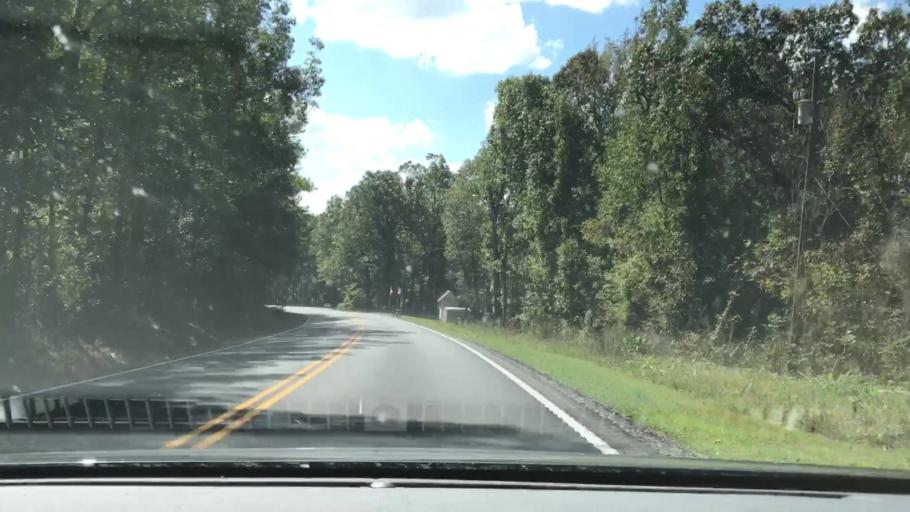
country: US
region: Kentucky
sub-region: Graves County
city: Mayfield
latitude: 36.8690
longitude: -88.5736
